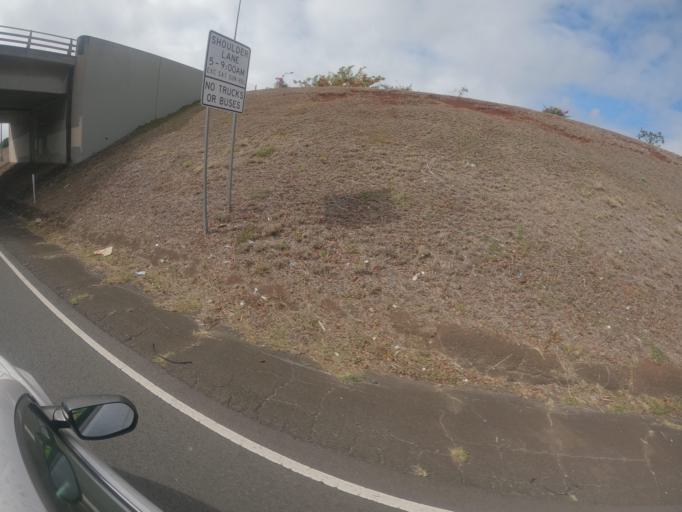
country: US
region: Hawaii
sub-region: Honolulu County
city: Waimalu
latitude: 21.3928
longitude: -157.9533
